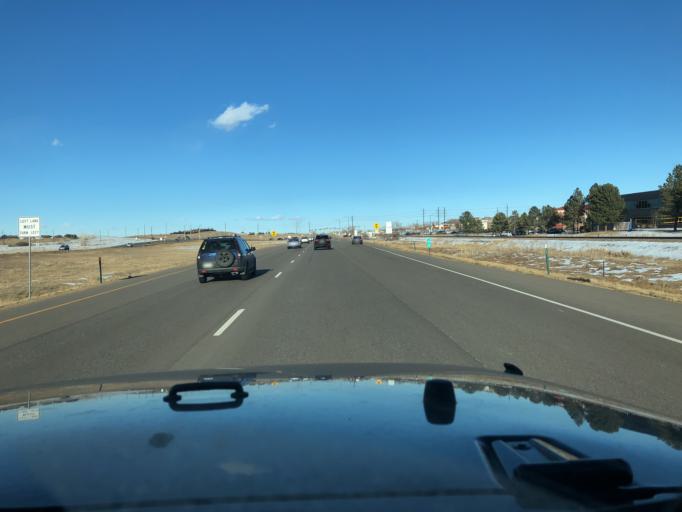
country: US
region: Colorado
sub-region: Boulder County
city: Gunbarrel
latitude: 40.0711
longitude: -105.2099
